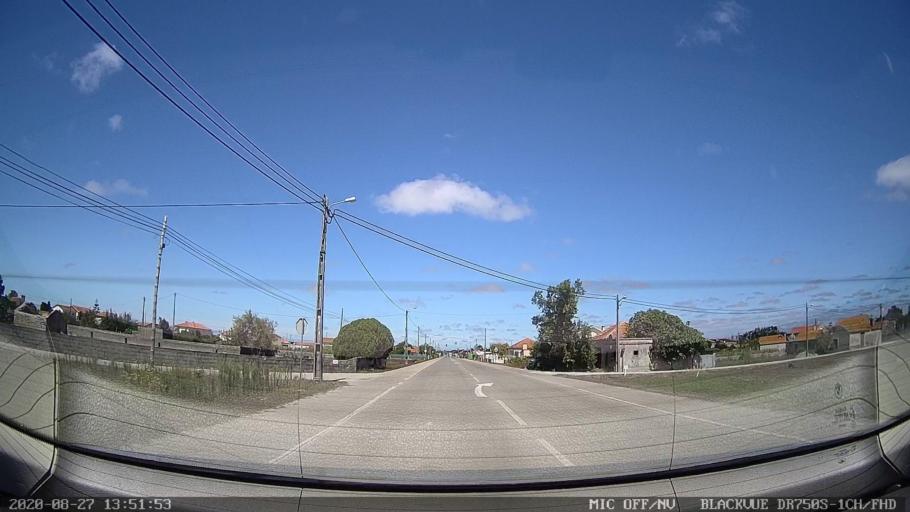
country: PT
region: Coimbra
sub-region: Mira
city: Mira
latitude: 40.3440
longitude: -8.7492
